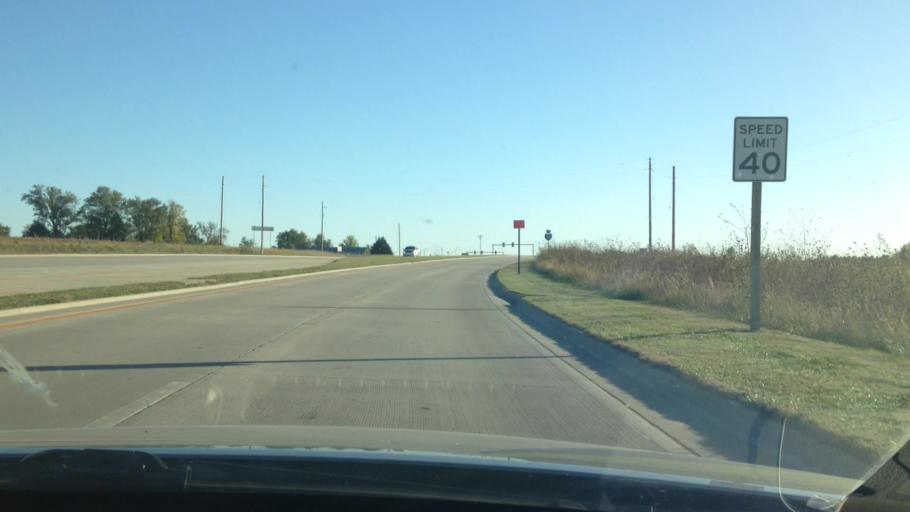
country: US
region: Kansas
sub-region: Johnson County
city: Edgerton
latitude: 38.7669
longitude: -94.9638
